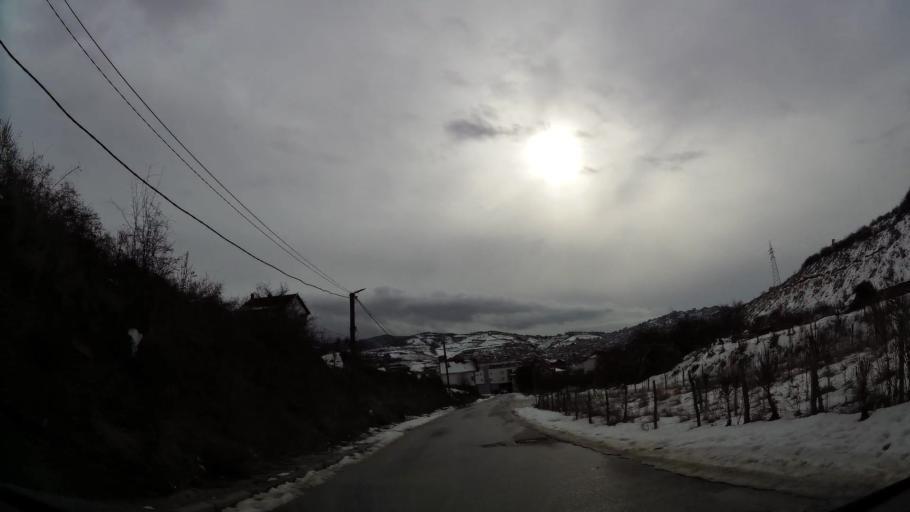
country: XK
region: Pristina
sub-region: Komuna e Prishtines
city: Pristina
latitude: 42.6907
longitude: 21.1771
